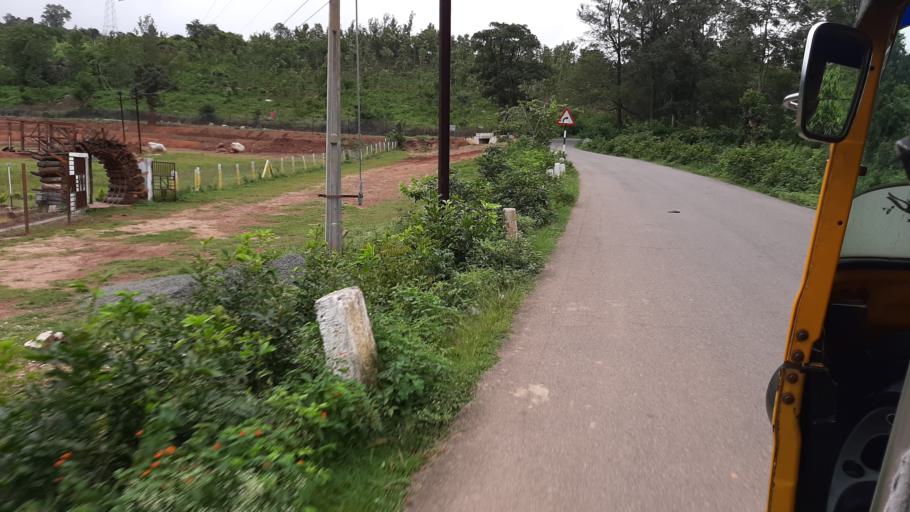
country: IN
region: Andhra Pradesh
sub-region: Vizianagaram District
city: Salur
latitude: 18.2413
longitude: 82.9991
